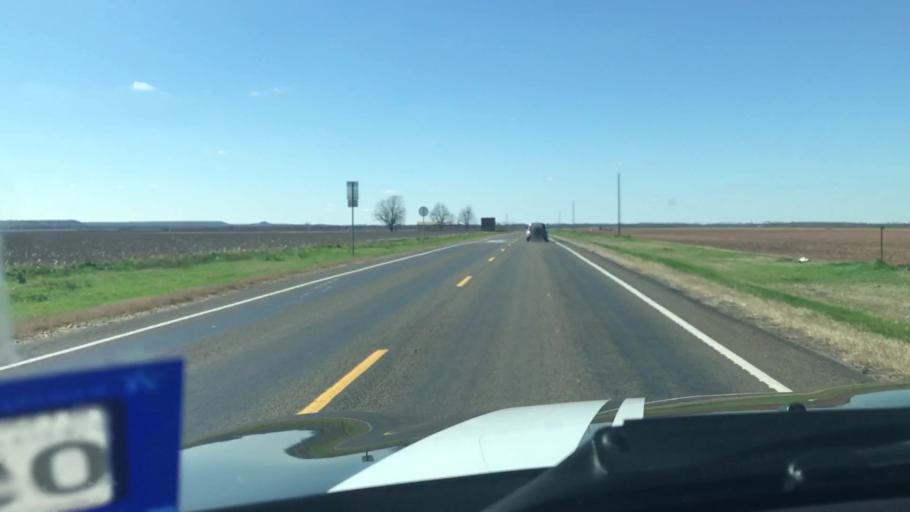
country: US
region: Texas
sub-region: Robertson County
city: Hearne
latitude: 30.8717
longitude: -96.6644
